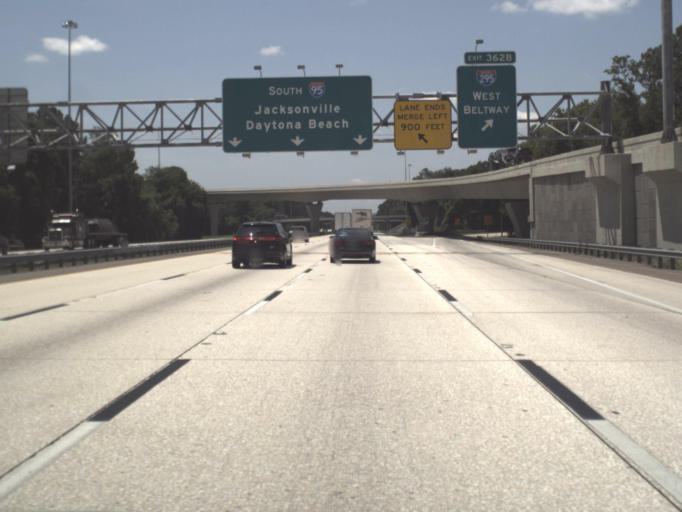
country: US
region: Florida
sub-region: Duval County
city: Jacksonville
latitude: 30.4641
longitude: -81.6483
